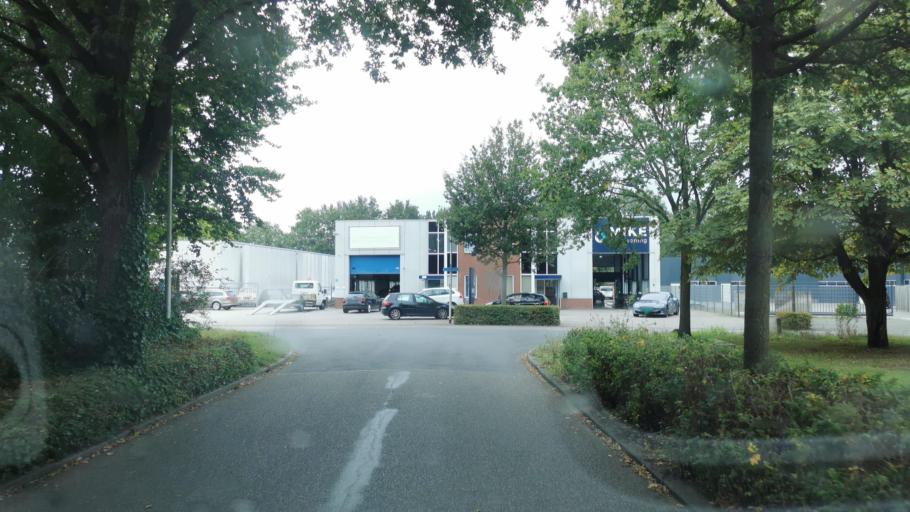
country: NL
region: Overijssel
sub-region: Gemeente Losser
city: Losser
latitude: 52.2502
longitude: 7.0136
